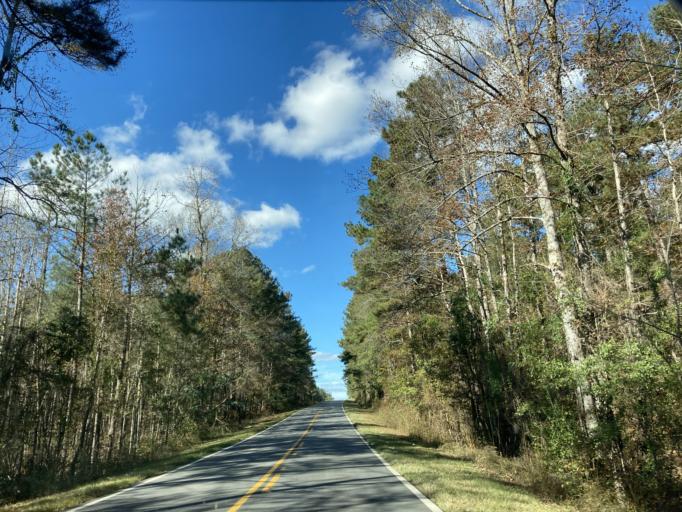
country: US
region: Georgia
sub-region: Jones County
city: Gray
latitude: 32.9344
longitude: -83.5053
